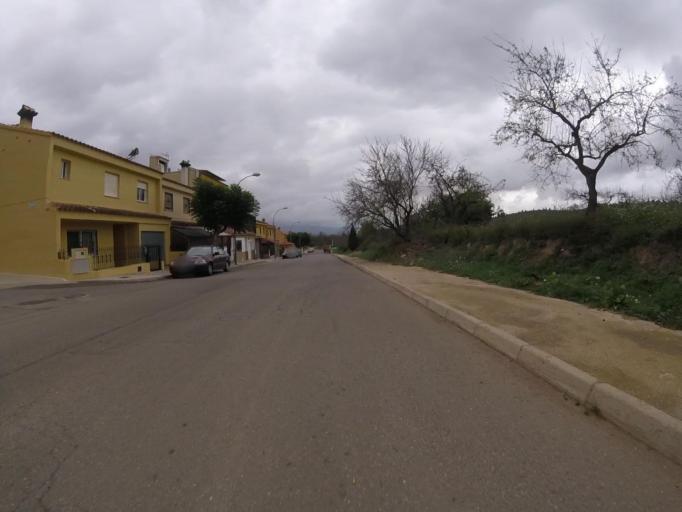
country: ES
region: Valencia
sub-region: Provincia de Castello
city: Cabanes
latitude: 40.1572
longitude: 0.0467
